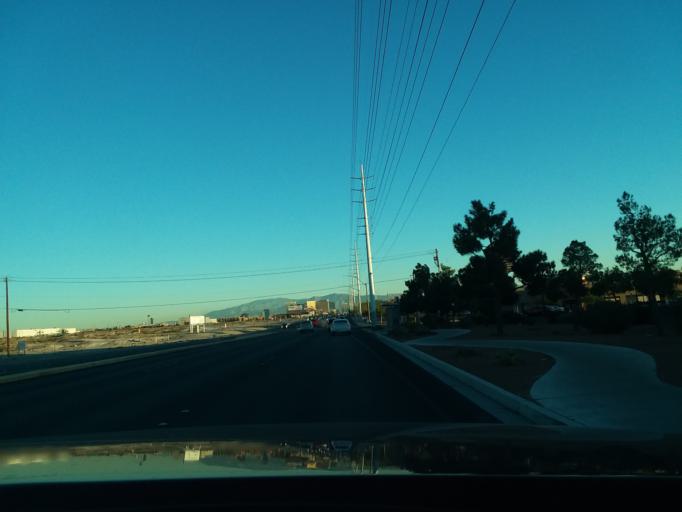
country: US
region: Nevada
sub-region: Clark County
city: Paradise
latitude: 36.0486
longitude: -115.1722
